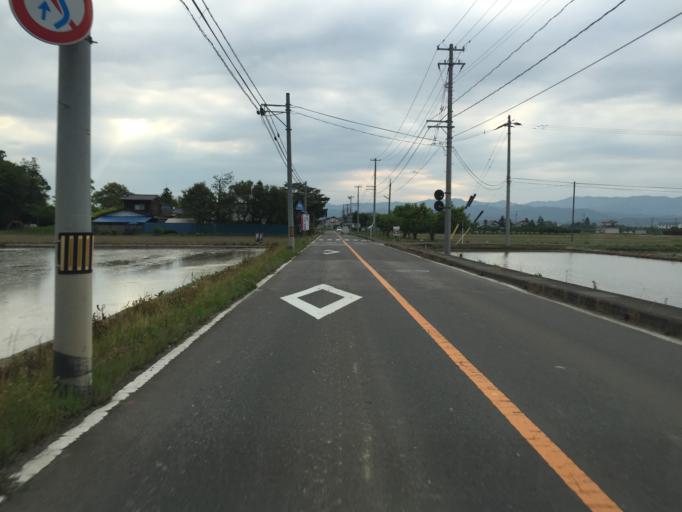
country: JP
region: Fukushima
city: Hobaramachi
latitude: 37.8501
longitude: 140.5470
